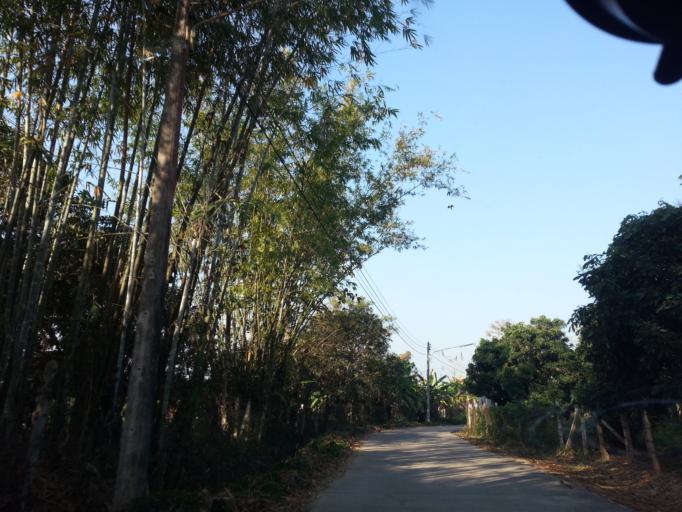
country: TH
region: Chiang Mai
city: San Sai
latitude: 18.8915
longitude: 99.1146
